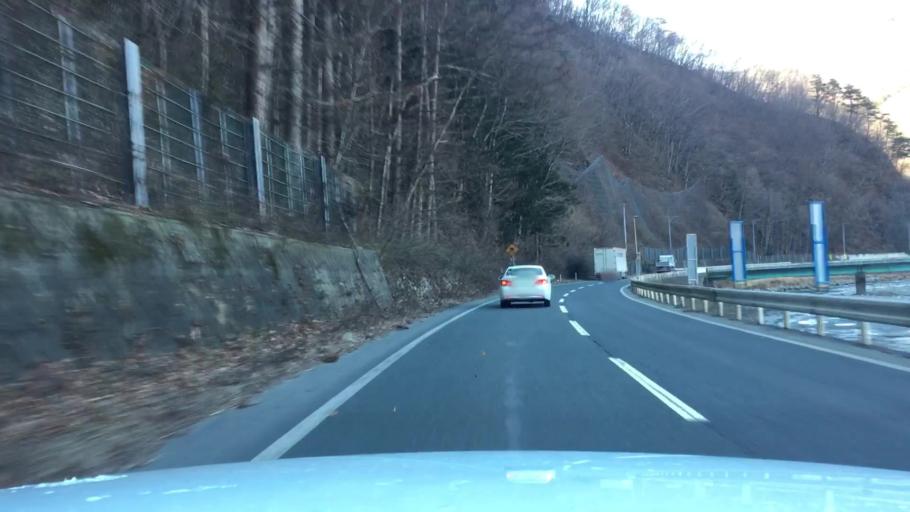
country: JP
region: Iwate
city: Miyako
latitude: 39.6037
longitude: 141.6528
